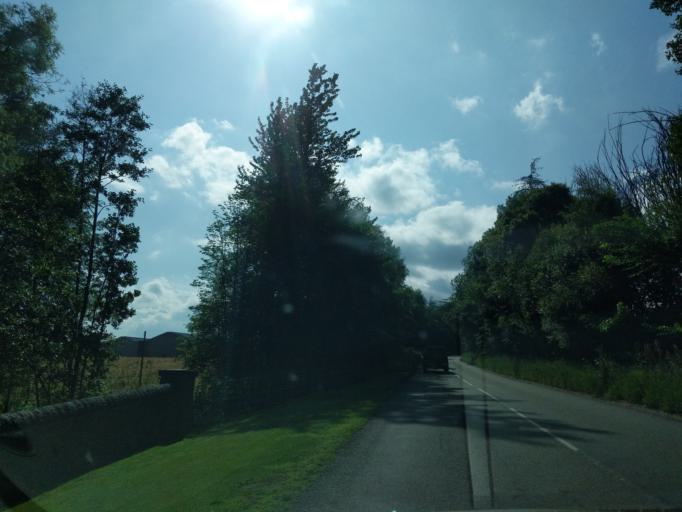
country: GB
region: Scotland
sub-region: Moray
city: Rothes
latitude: 57.4904
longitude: -3.2038
